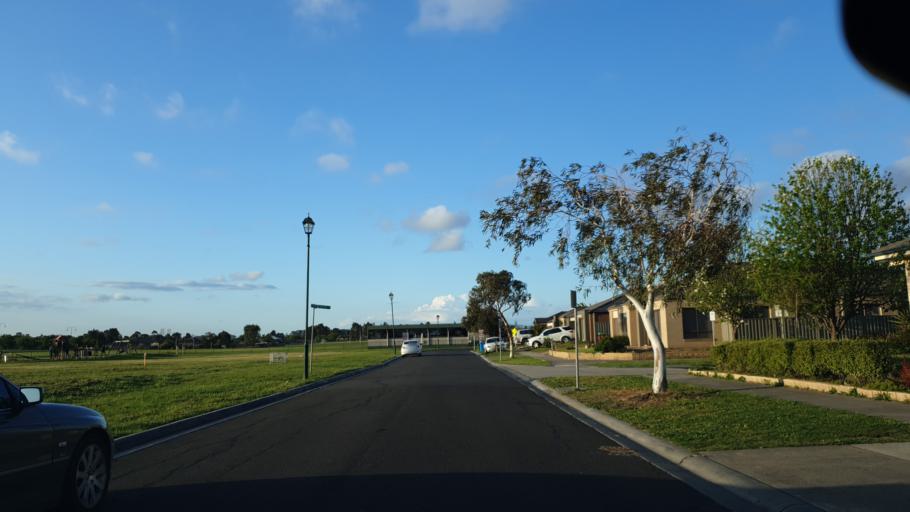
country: AU
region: Victoria
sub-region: Casey
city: Cranbourne East
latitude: -38.1073
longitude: 145.3033
